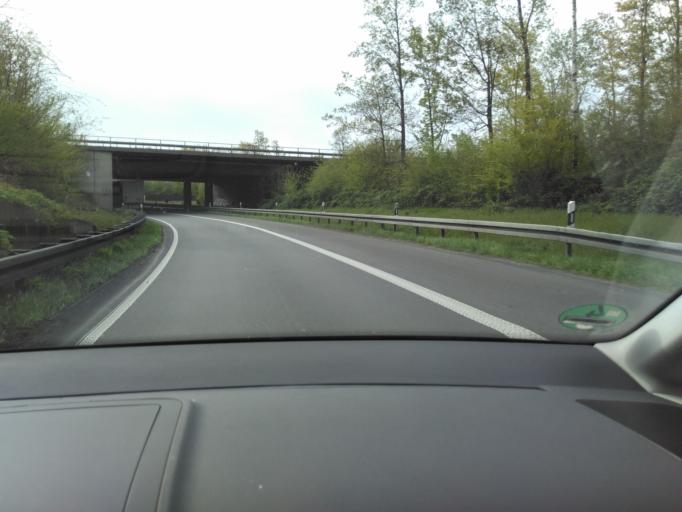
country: DE
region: North Rhine-Westphalia
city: Meiderich
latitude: 51.4883
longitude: 6.8167
